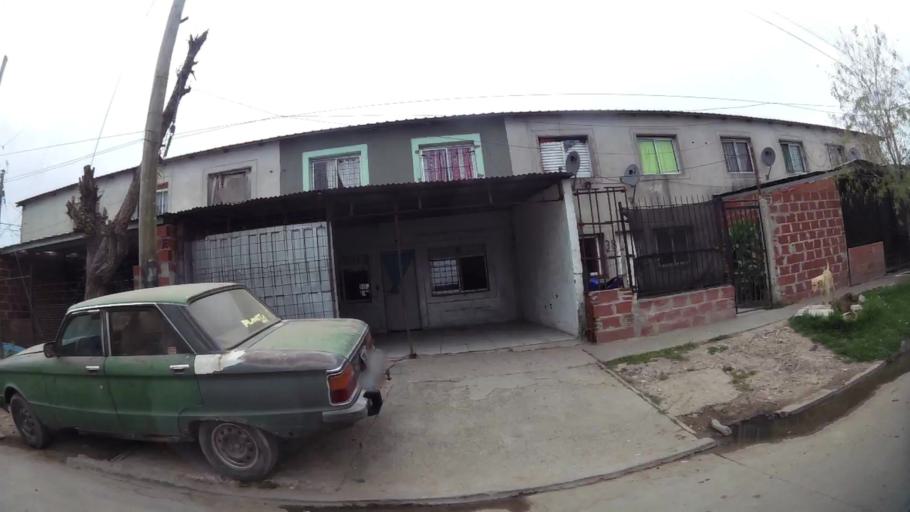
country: AR
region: Buenos Aires
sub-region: Partido de Campana
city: Campana
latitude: -34.1833
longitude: -58.9361
